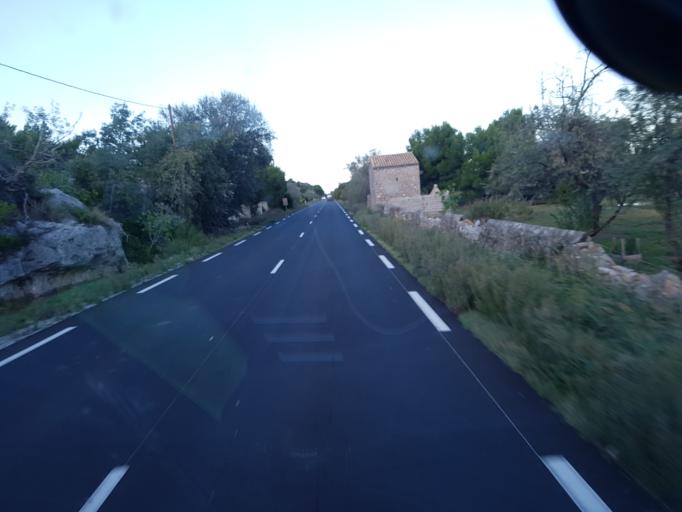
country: FR
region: Languedoc-Roussillon
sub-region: Departement de l'Aude
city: Port-la-Nouvelle
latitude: 42.9891
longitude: 3.0357
